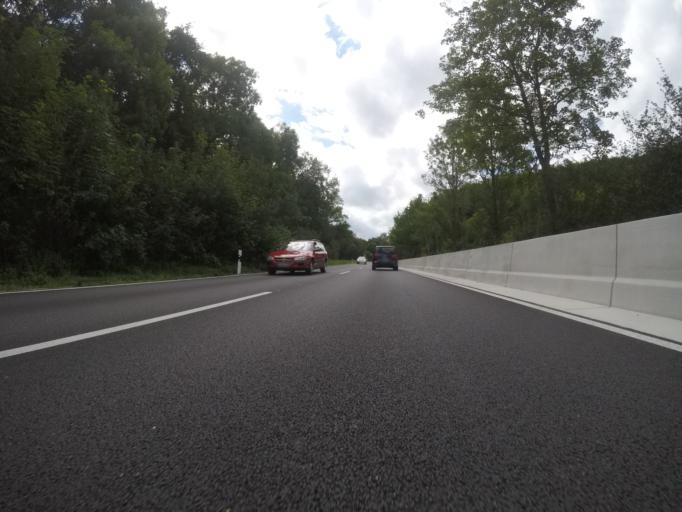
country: DE
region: Baden-Wuerttemberg
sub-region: Regierungsbezirk Stuttgart
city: Renningen
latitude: 48.7572
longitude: 8.9261
